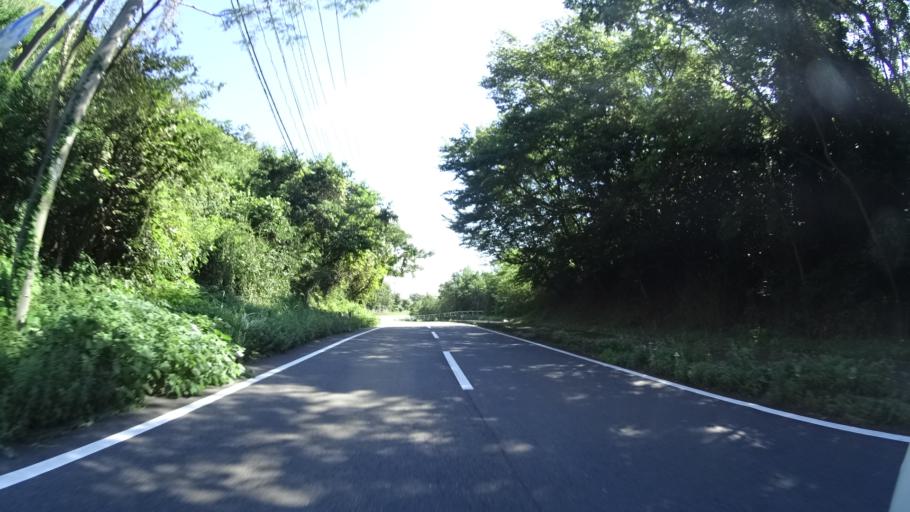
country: JP
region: Oita
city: Beppu
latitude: 33.3297
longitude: 131.4539
